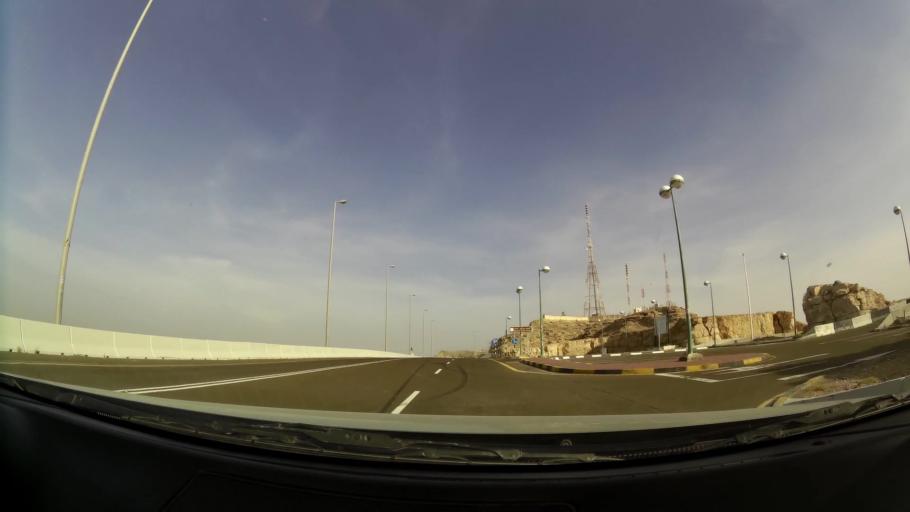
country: AE
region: Abu Dhabi
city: Al Ain
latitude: 24.0777
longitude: 55.7717
